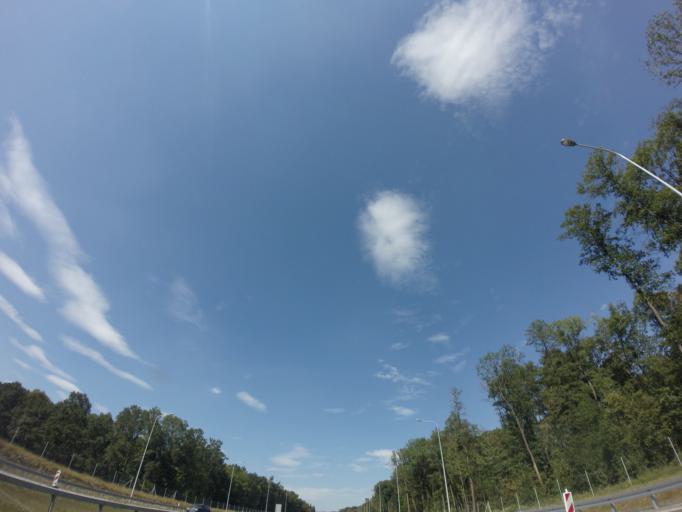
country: PL
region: Lower Silesian Voivodeship
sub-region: Legnica
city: Legnica
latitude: 51.2876
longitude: 16.1524
